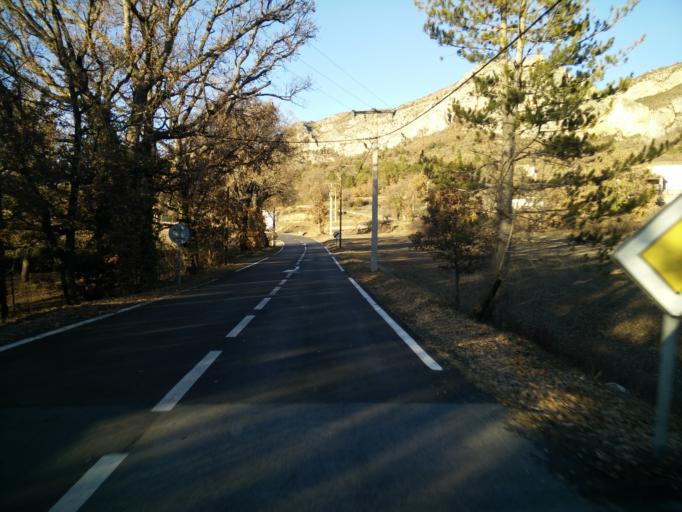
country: FR
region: Provence-Alpes-Cote d'Azur
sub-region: Departement des Alpes-de-Haute-Provence
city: Riez
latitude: 43.8296
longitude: 6.2250
